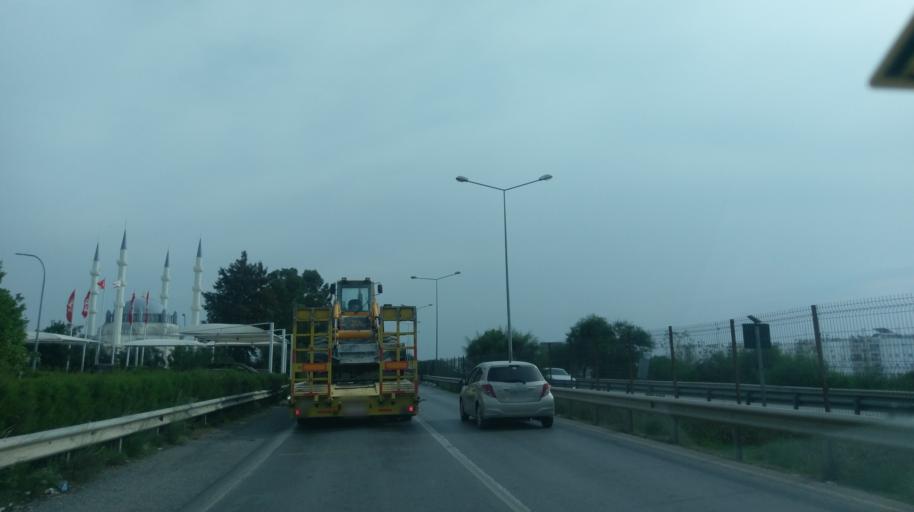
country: CY
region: Lefkosia
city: Nicosia
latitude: 35.2170
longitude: 33.4200
